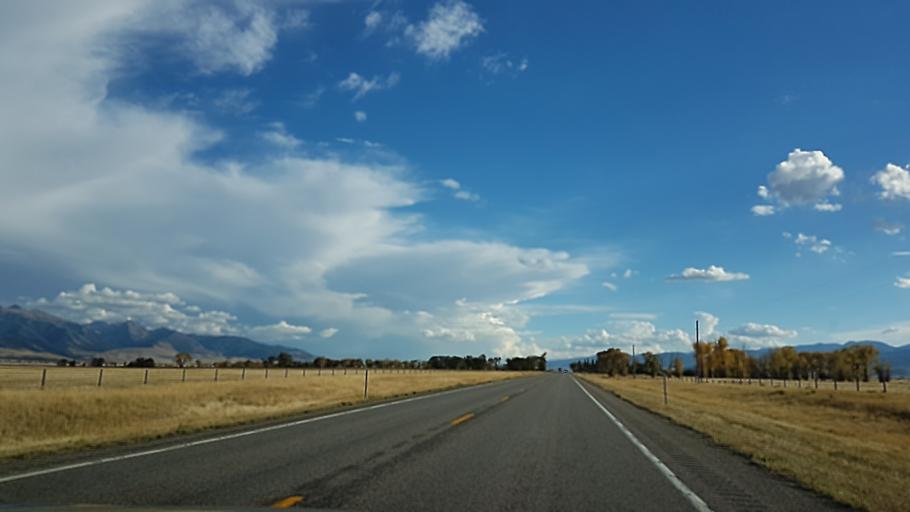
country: US
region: Montana
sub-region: Madison County
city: Virginia City
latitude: 45.2100
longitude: -111.6788
